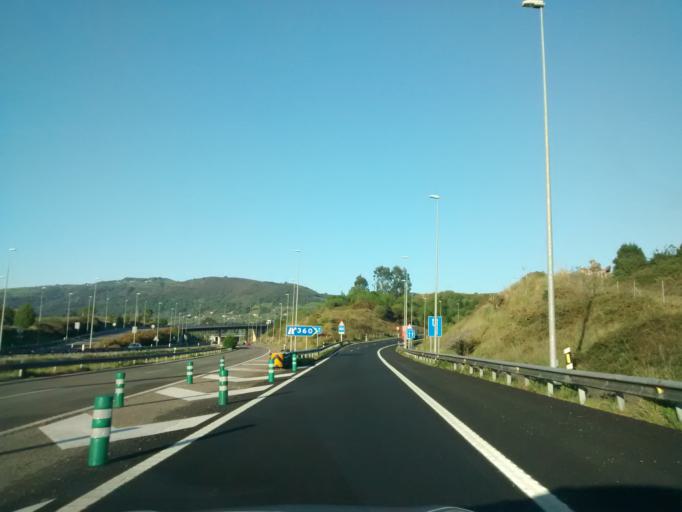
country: ES
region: Asturias
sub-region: Province of Asturias
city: Villaviciosa
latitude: 43.4675
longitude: -5.4844
